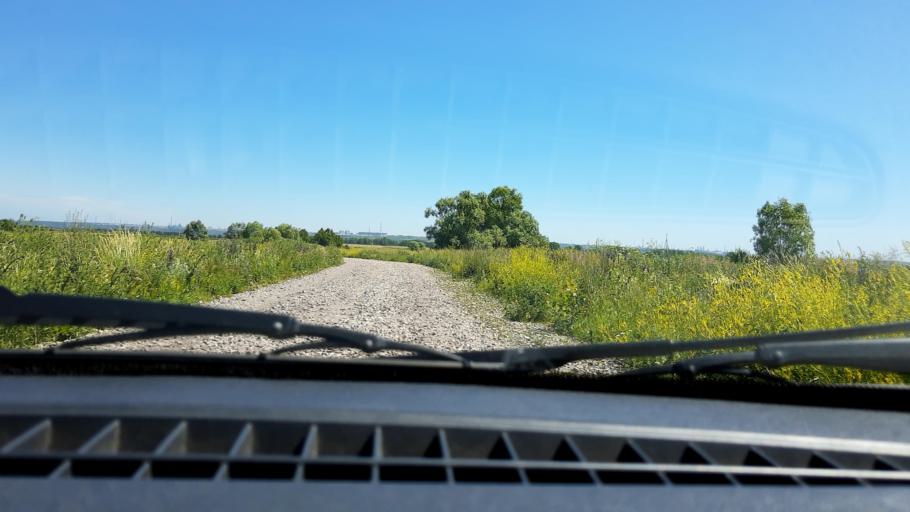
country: RU
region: Bashkortostan
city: Mikhaylovka
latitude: 54.8753
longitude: 55.9353
